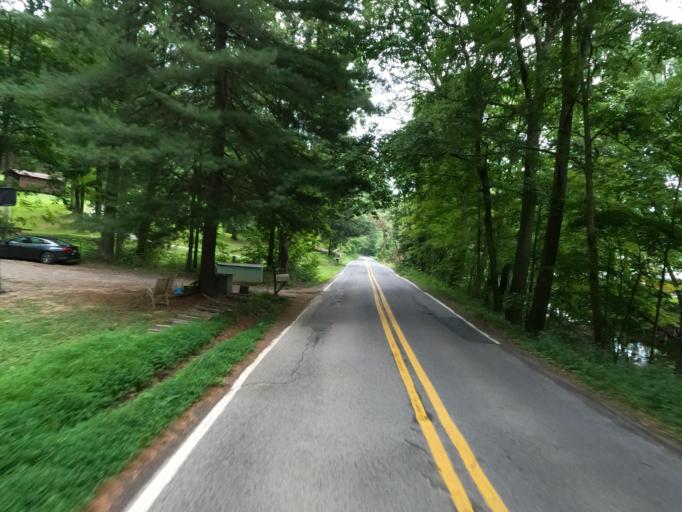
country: US
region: West Virginia
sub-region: Marion County
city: Fairmont
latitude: 39.5002
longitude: -80.0975
